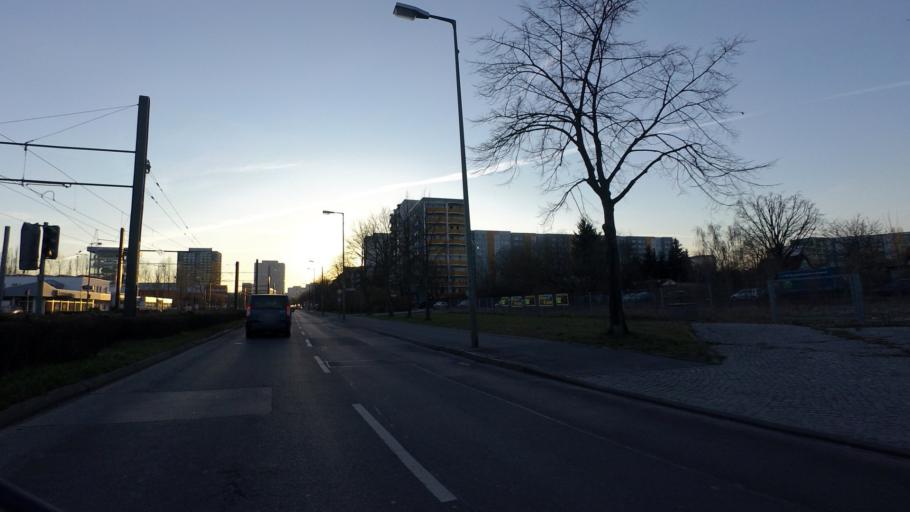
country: DE
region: Berlin
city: Marzahn
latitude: 52.5341
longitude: 13.5559
